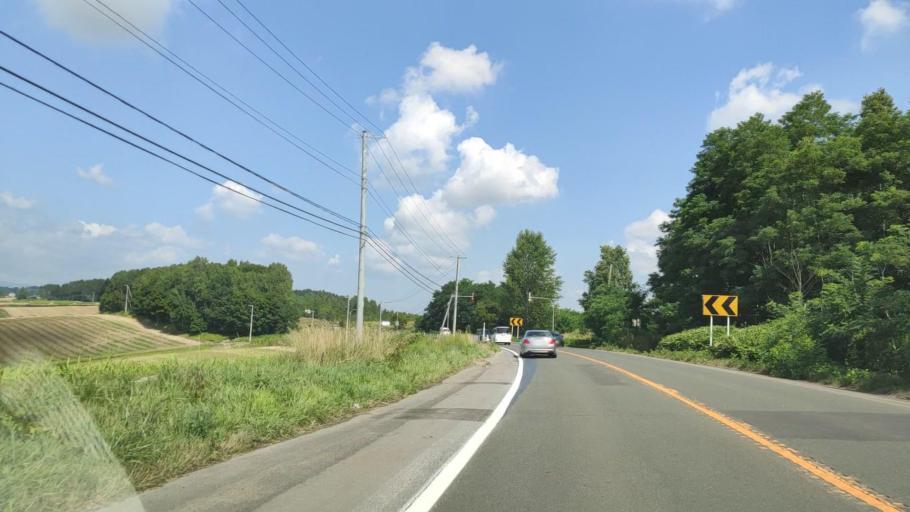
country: JP
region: Hokkaido
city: Shimo-furano
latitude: 43.5050
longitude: 142.4588
